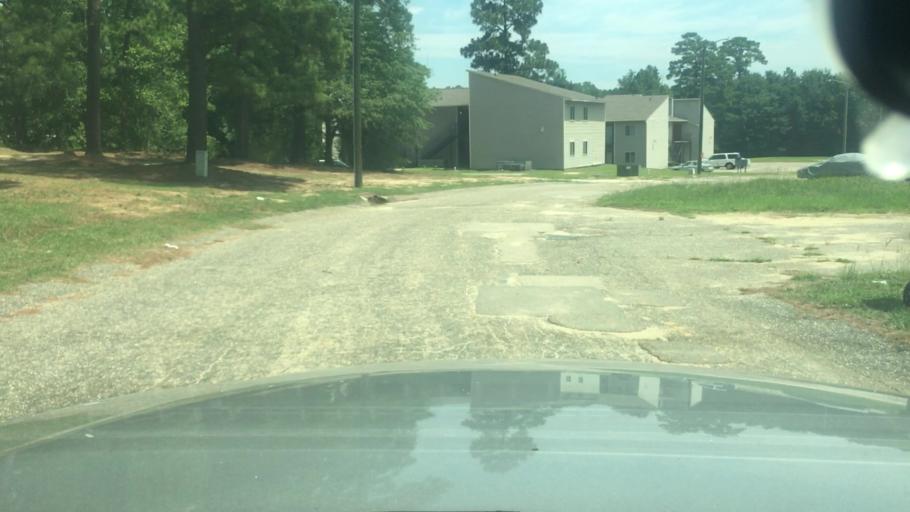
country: US
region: North Carolina
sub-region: Hoke County
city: Rockfish
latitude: 35.0380
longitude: -78.9954
